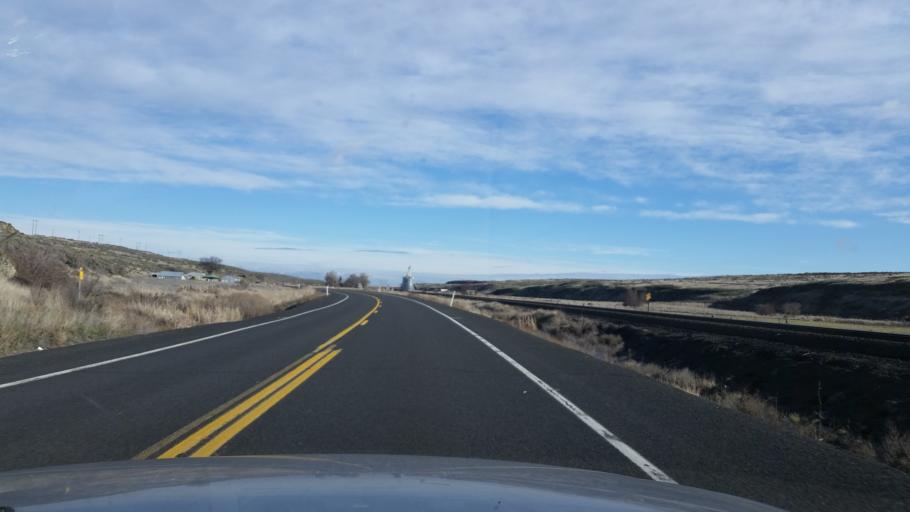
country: US
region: Washington
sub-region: Adams County
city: Ritzville
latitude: 47.3574
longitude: -118.4982
